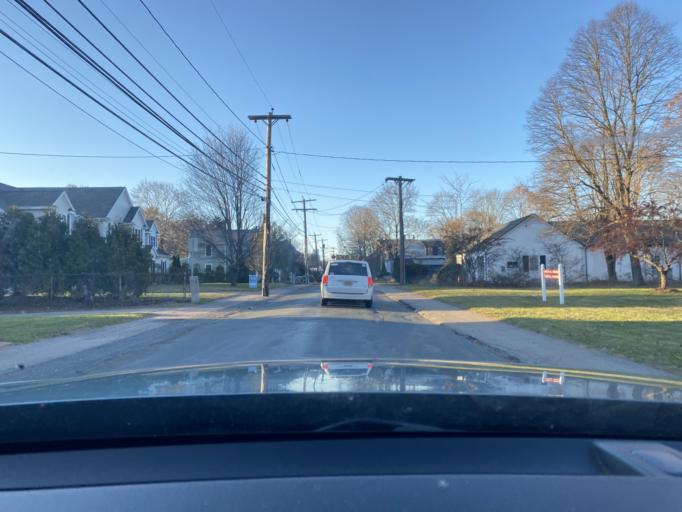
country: US
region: Massachusetts
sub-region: Norfolk County
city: Medfield
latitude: 42.1852
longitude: -71.3036
